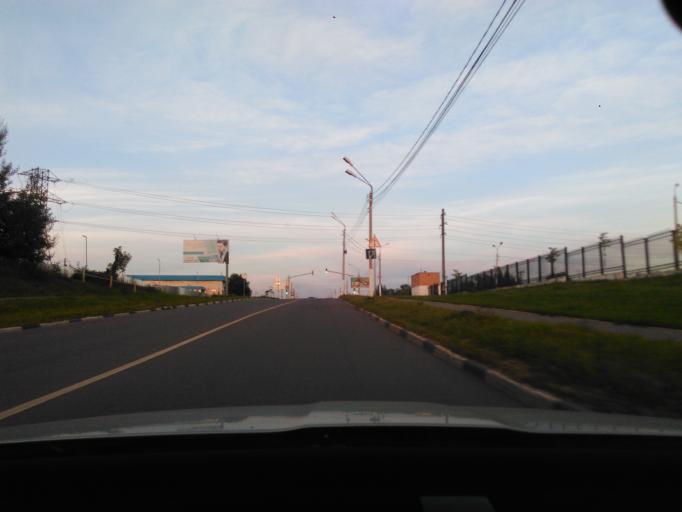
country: RU
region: Moskovskaya
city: Klin
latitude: 56.3174
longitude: 36.7411
